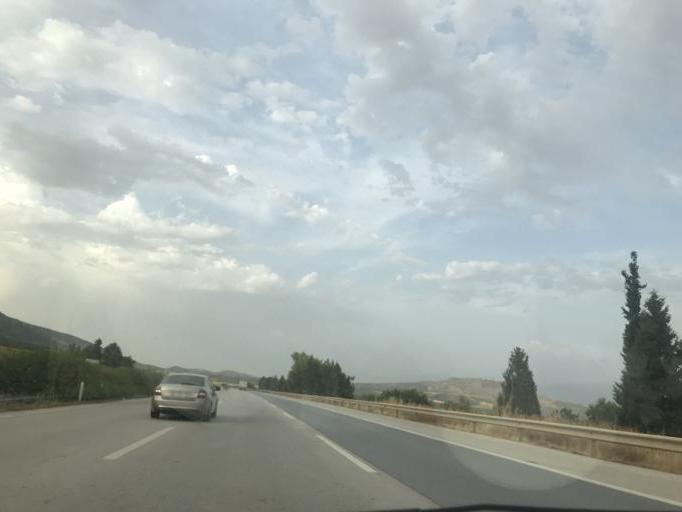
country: TR
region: Adana
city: Kosreli
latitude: 37.0167
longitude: 36.0050
